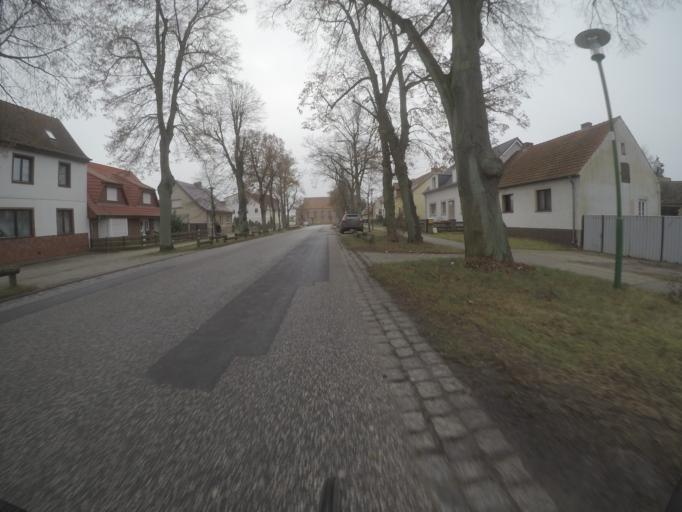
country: DE
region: Brandenburg
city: Marienwerder
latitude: 52.8434
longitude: 13.5986
